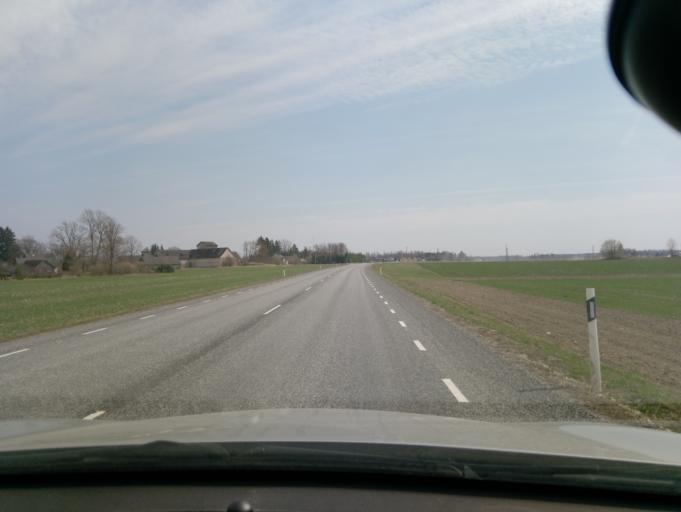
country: EE
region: Jaervamaa
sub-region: Tueri vald
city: Sarevere
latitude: 58.7631
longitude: 25.5449
